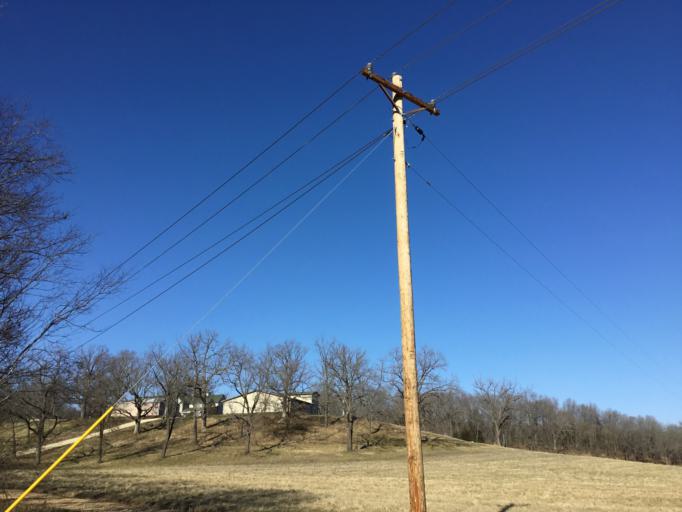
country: US
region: Missouri
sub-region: Maries County
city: Belle
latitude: 38.3656
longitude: -91.6818
